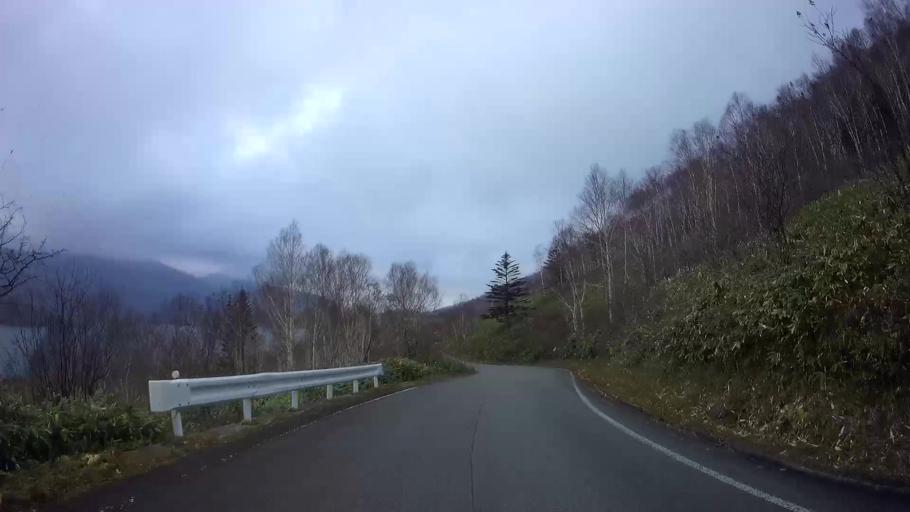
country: JP
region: Gunma
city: Nakanojomachi
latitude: 36.6958
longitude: 138.6565
